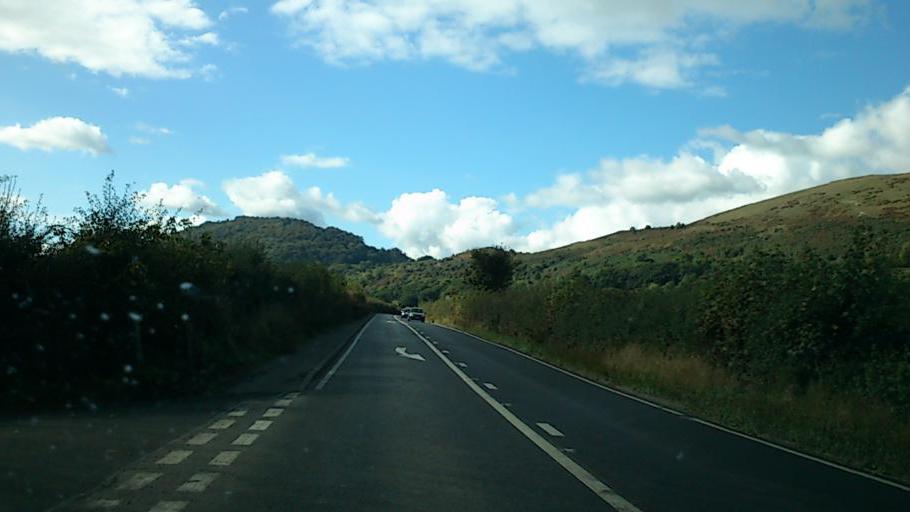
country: GB
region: England
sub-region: Shropshire
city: Westbury
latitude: 52.7073
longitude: -3.0151
